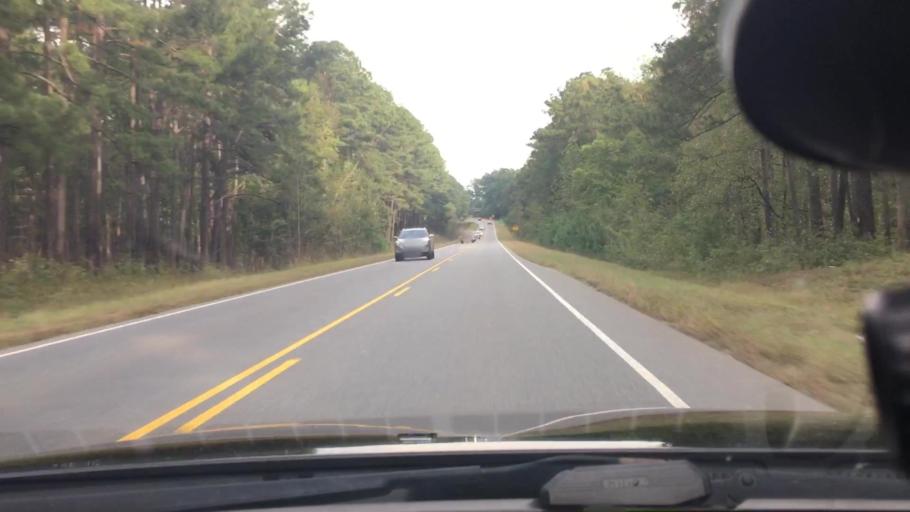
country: US
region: North Carolina
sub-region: Montgomery County
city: Troy
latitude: 35.3222
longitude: -79.9527
